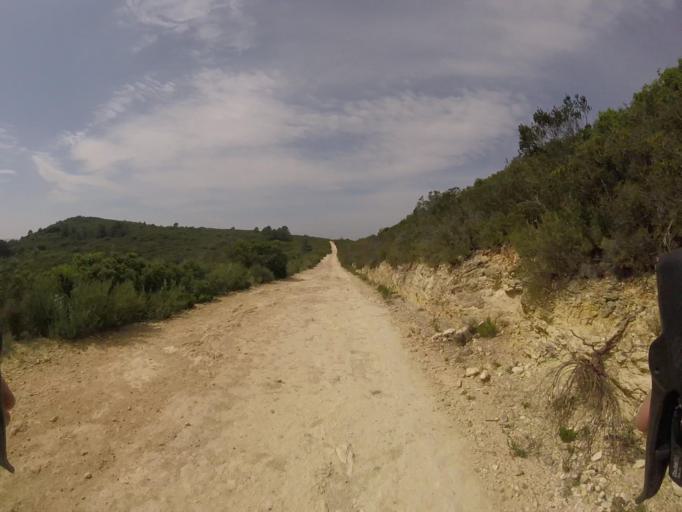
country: ES
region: Valencia
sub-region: Provincia de Castello
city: Cuevas de Vinroma
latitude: 40.2612
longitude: 0.1122
